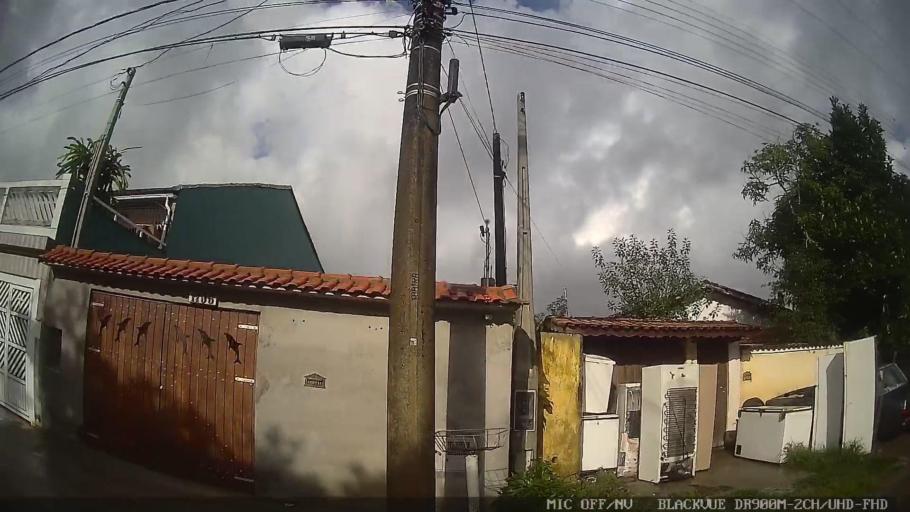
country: BR
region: Sao Paulo
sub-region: Itanhaem
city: Itanhaem
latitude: -24.2242
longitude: -46.8895
